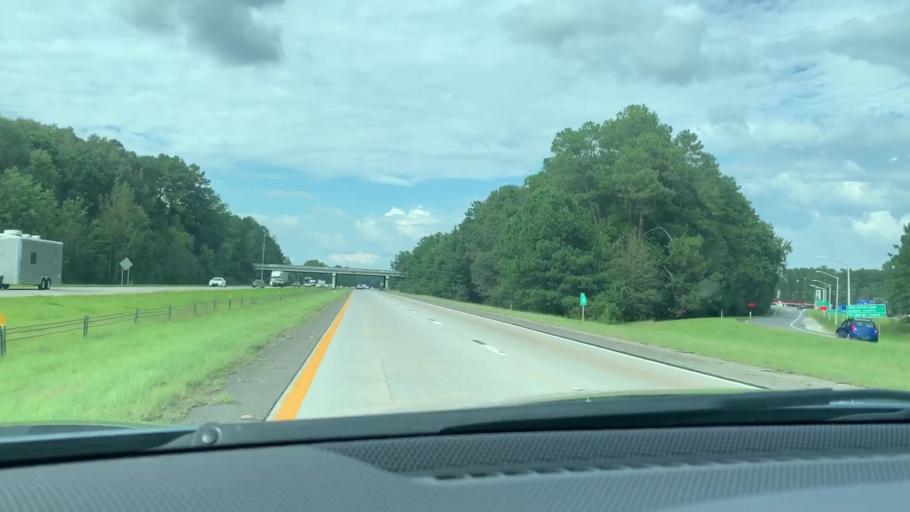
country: US
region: South Carolina
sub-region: Jasper County
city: Hardeeville
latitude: 32.3098
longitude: -81.0596
